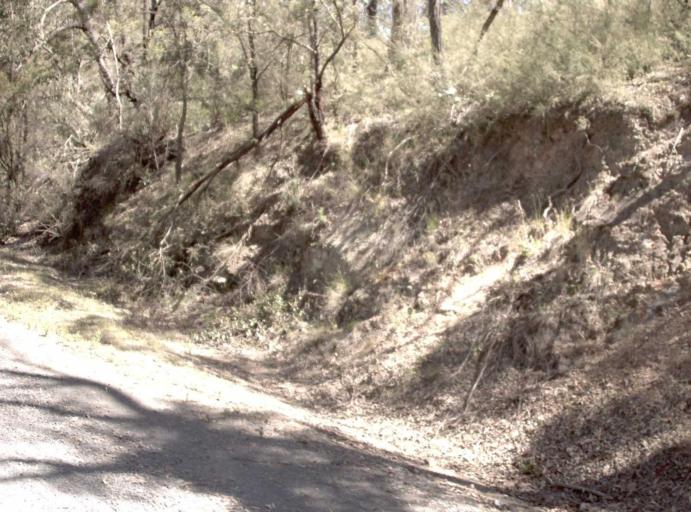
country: AU
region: New South Wales
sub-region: Bombala
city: Bombala
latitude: -37.1000
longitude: 148.6338
